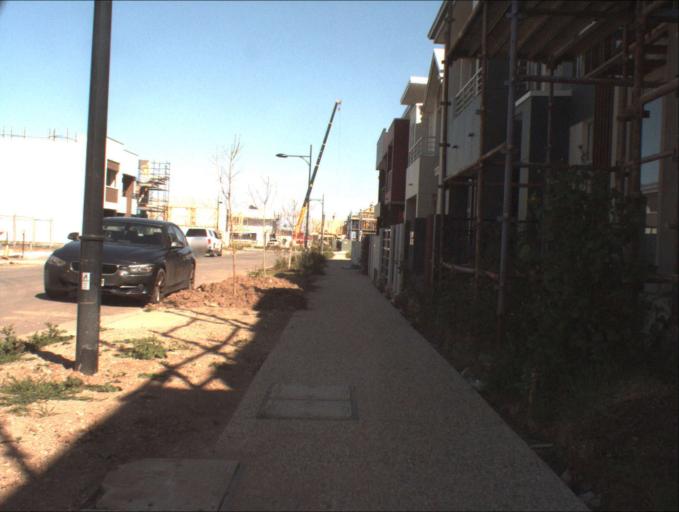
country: AU
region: South Australia
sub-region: Port Adelaide Enfield
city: Klemzig
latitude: -34.8636
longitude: 138.6211
